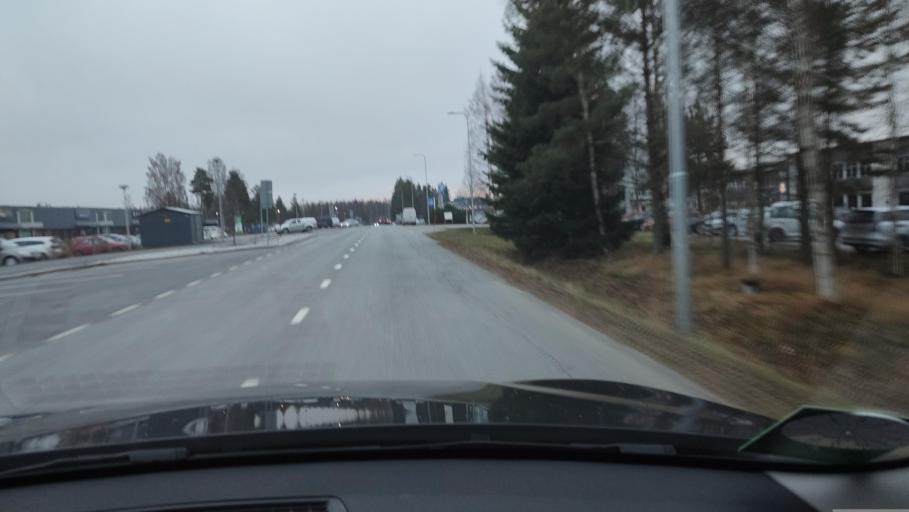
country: FI
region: Southern Ostrobothnia
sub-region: Suupohja
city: Kauhajoki
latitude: 62.4593
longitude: 22.1989
